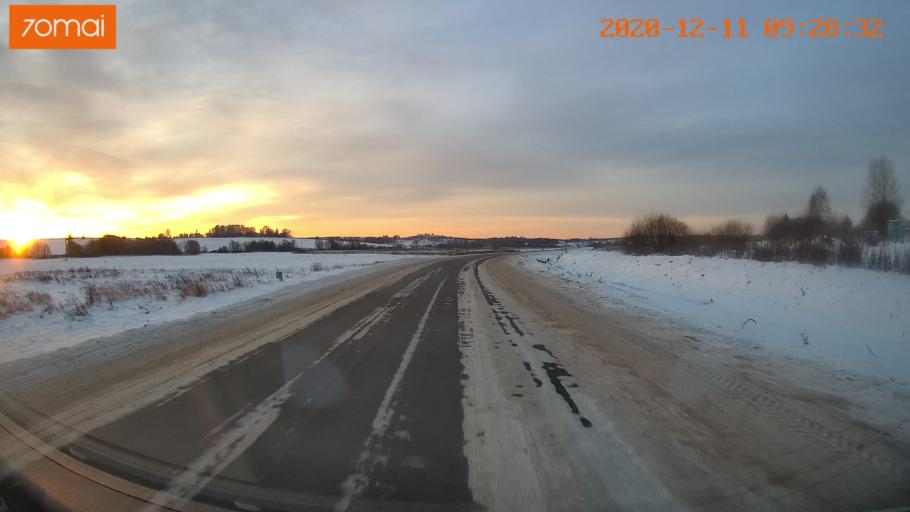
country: RU
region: Vologda
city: Vologda
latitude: 59.1519
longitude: 40.0078
